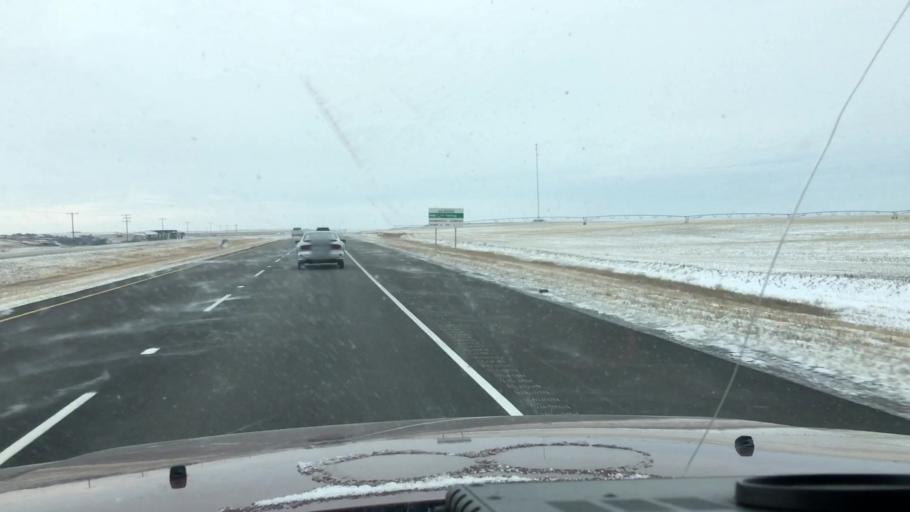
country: CA
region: Saskatchewan
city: Saskatoon
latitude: 51.7463
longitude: -106.4764
